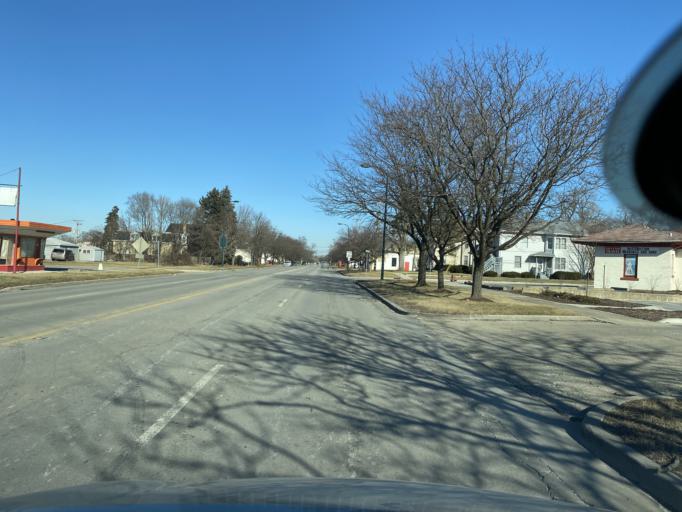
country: US
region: Illinois
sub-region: Will County
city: Lockport
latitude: 41.5910
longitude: -88.0566
